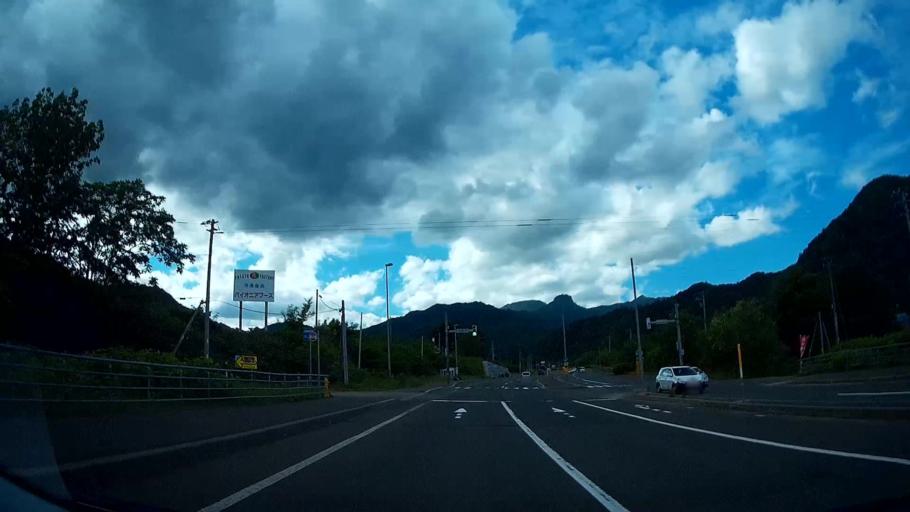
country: JP
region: Hokkaido
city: Sapporo
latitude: 42.9618
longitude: 141.2226
